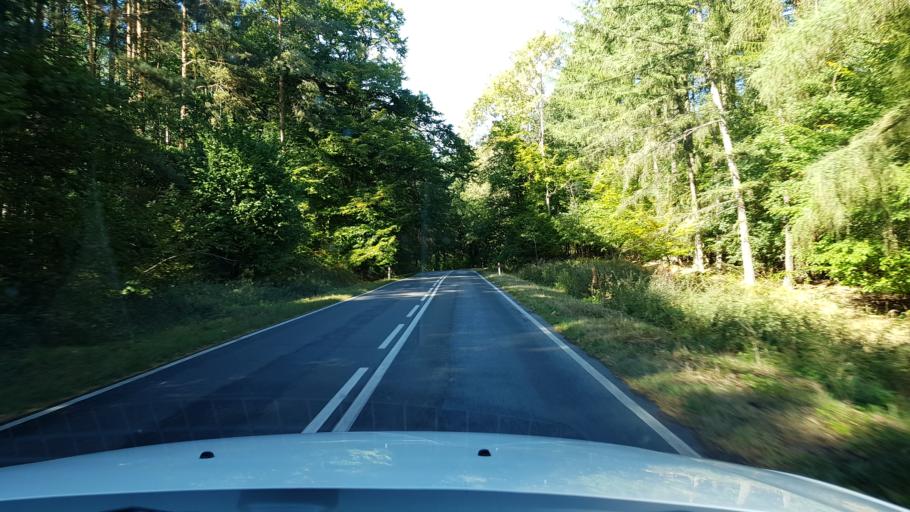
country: PL
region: West Pomeranian Voivodeship
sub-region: Powiat gryfinski
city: Gryfino
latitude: 53.1945
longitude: 14.5245
